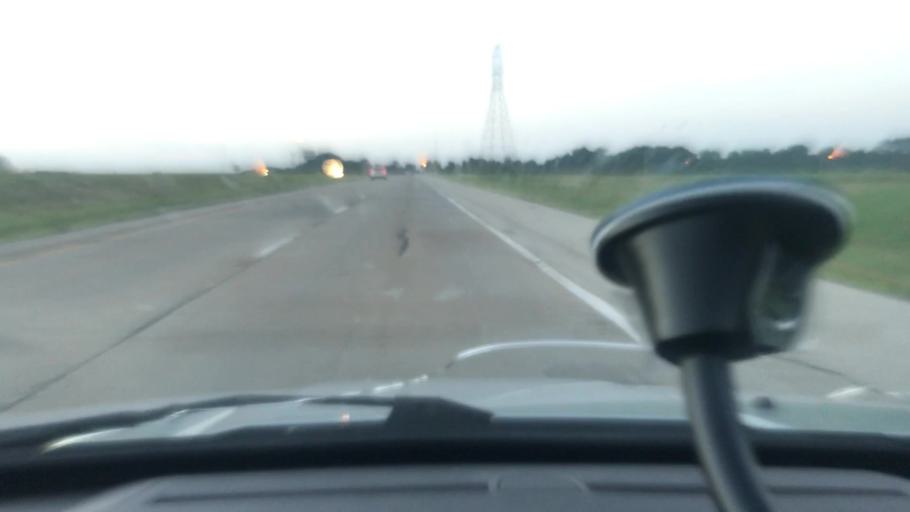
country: US
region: Illinois
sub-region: Peoria County
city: Bellevue
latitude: 40.7382
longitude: -89.6693
